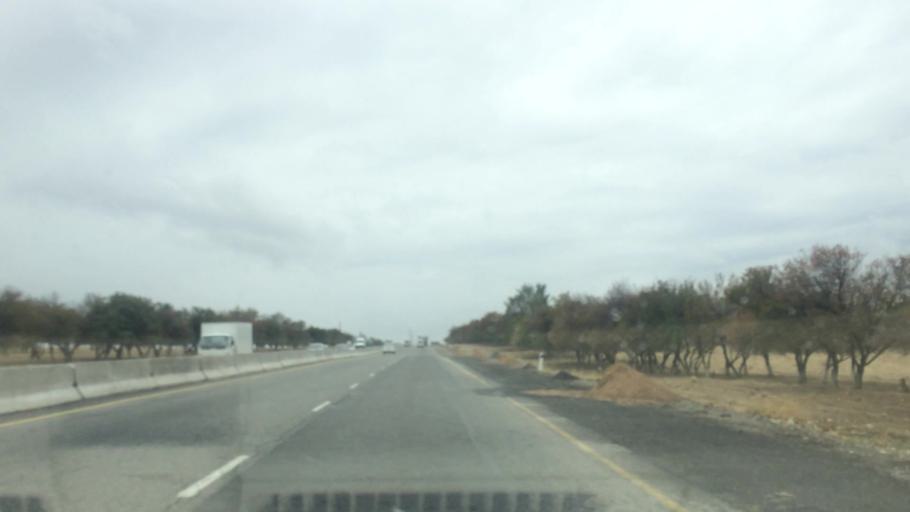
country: UZ
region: Samarqand
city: Bulung'ur
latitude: 39.8578
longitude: 67.4681
